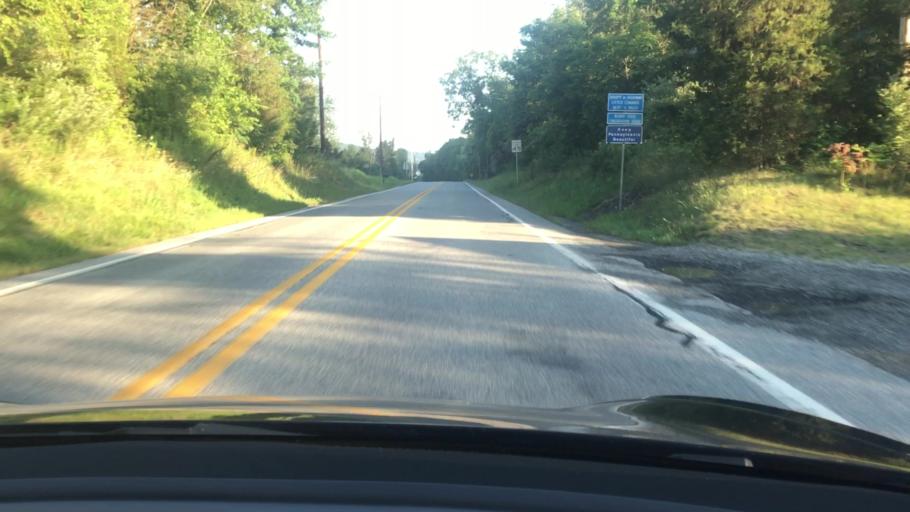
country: US
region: Pennsylvania
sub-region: York County
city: Valley Green
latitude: 40.0988
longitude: -76.8729
